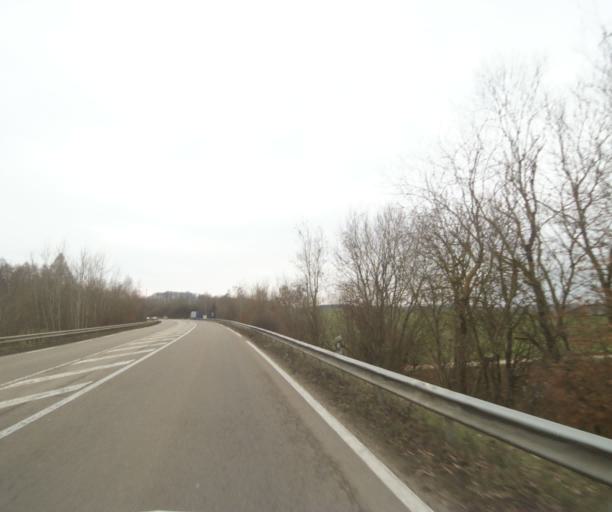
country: FR
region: Champagne-Ardenne
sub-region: Departement de la Haute-Marne
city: Bienville
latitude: 48.5821
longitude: 5.0286
